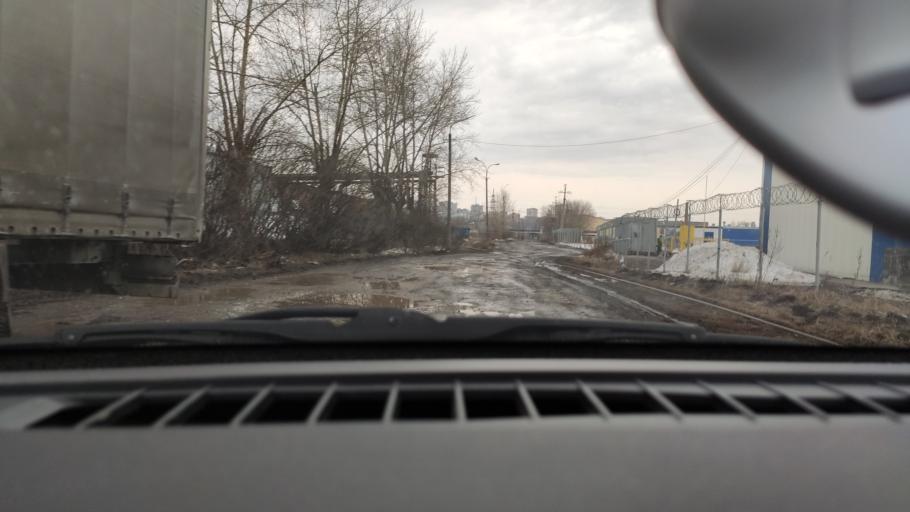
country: RU
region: Perm
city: Perm
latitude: 58.0461
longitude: 56.3147
